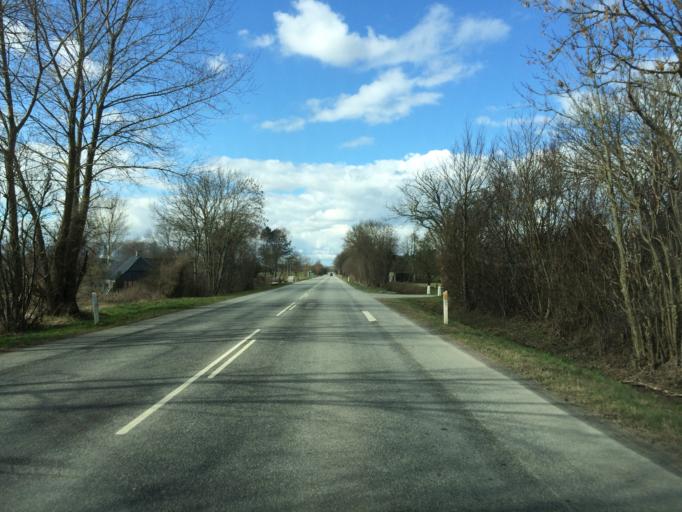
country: DK
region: South Denmark
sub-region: Assens Kommune
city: Arup
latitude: 55.4318
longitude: 10.0110
